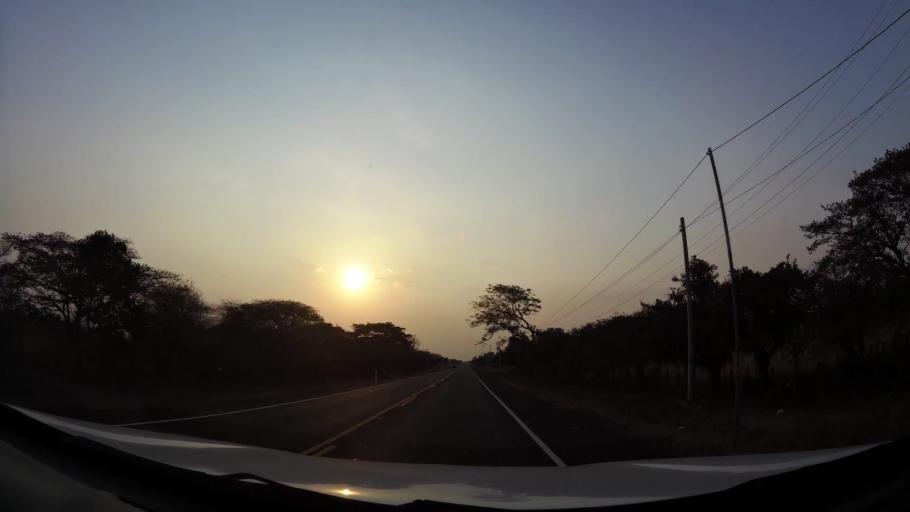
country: NI
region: Leon
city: La Paz Centro
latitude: 12.3193
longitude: -86.6143
